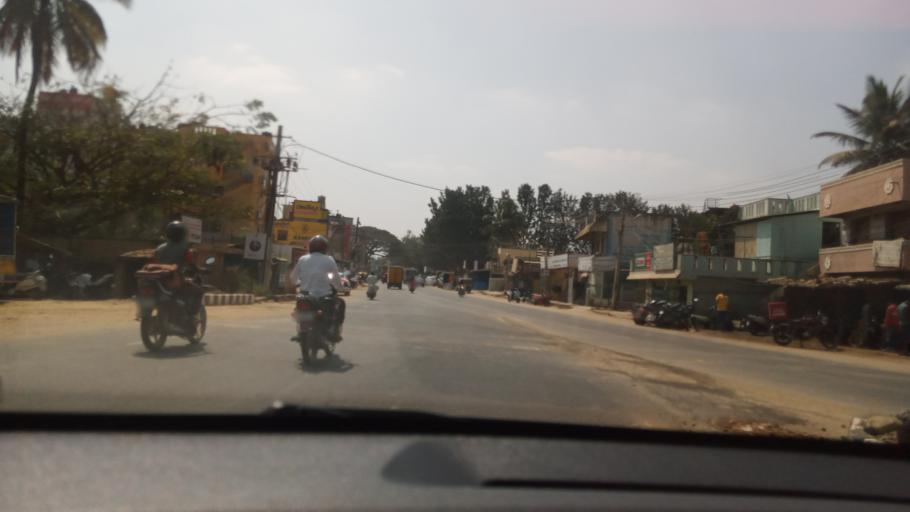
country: IN
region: Karnataka
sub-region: Bangalore Rural
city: Hoskote
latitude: 12.9447
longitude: 77.7471
